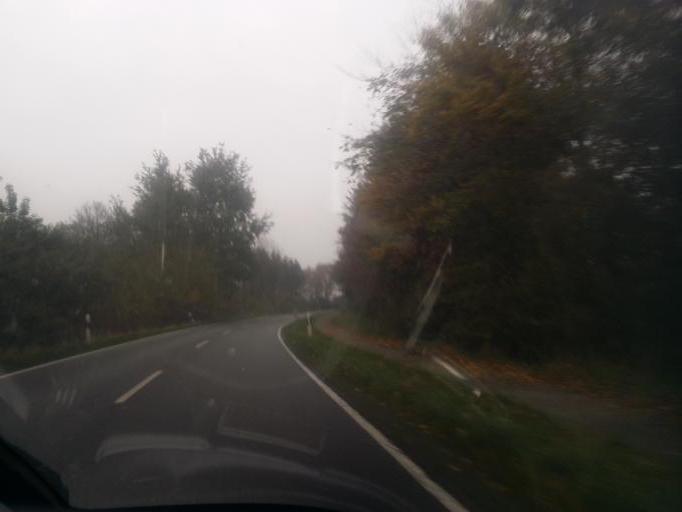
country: DE
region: Schleswig-Holstein
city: Sieverstedt
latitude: 54.6781
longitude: 9.4857
